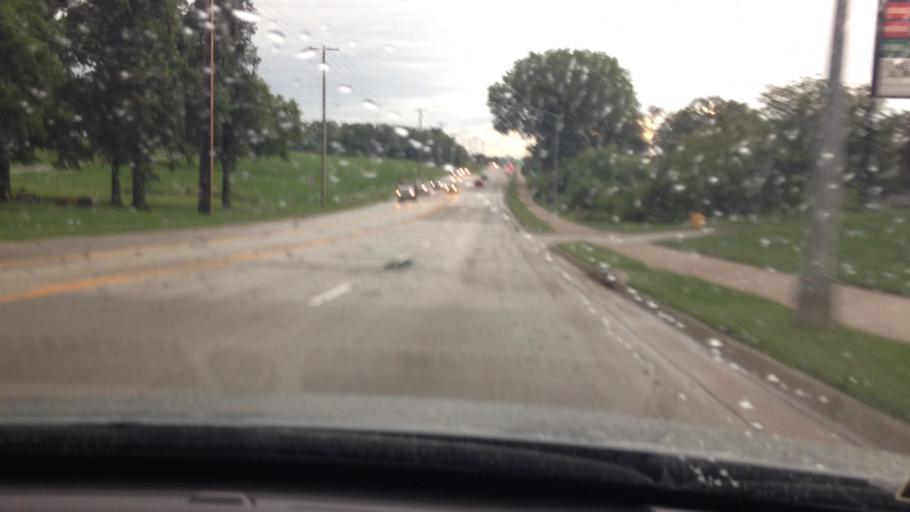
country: US
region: Kansas
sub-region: Leavenworth County
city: Lansing
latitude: 39.2671
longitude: -94.9191
